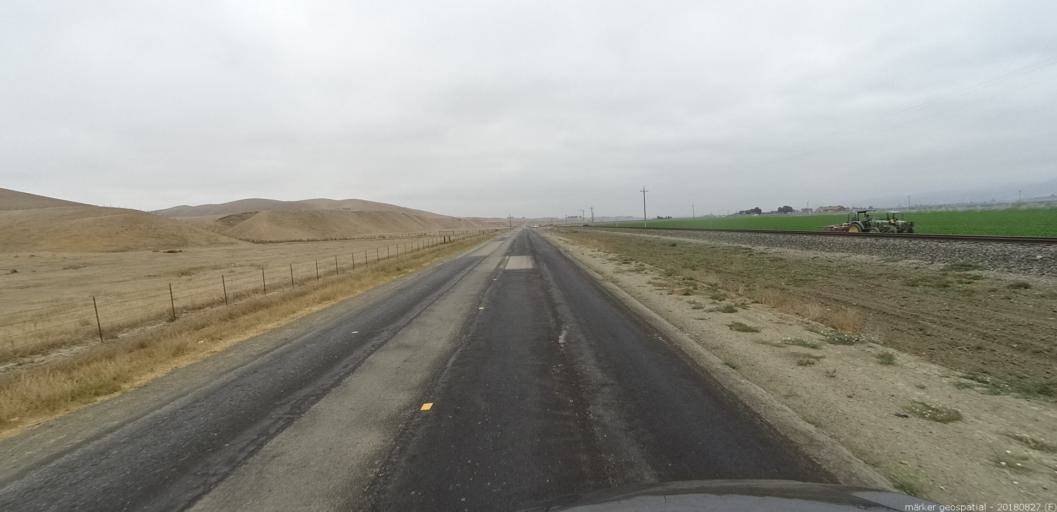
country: US
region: California
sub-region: Monterey County
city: Greenfield
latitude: 36.3068
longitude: -121.1649
